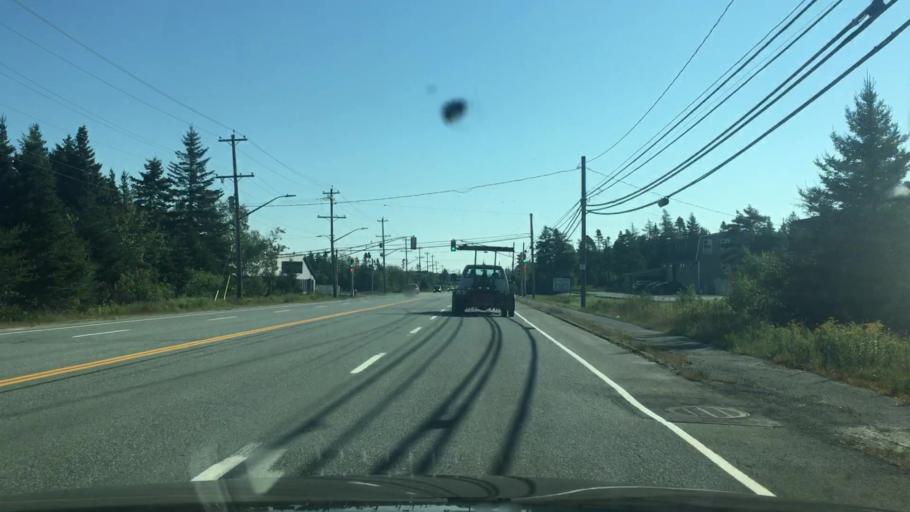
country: CA
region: Nova Scotia
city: Cole Harbour
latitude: 44.7012
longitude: -63.4797
